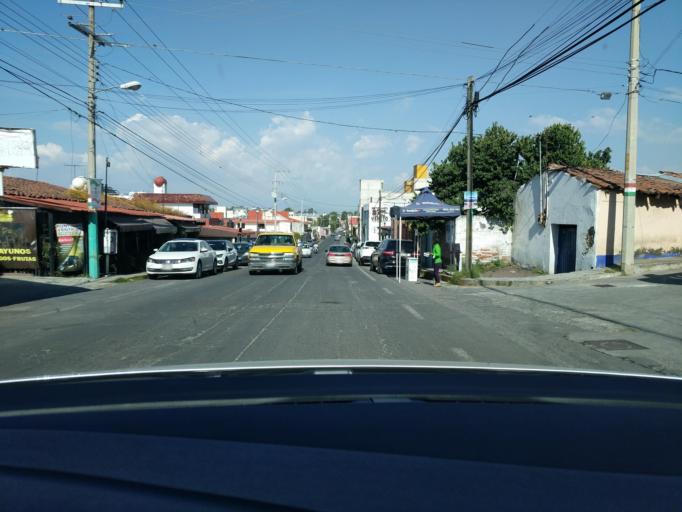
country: MX
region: Puebla
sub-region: San Gregorio Atzompa
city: Chipilo de Francisco Javier Mina
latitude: 19.0062
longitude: -98.3309
